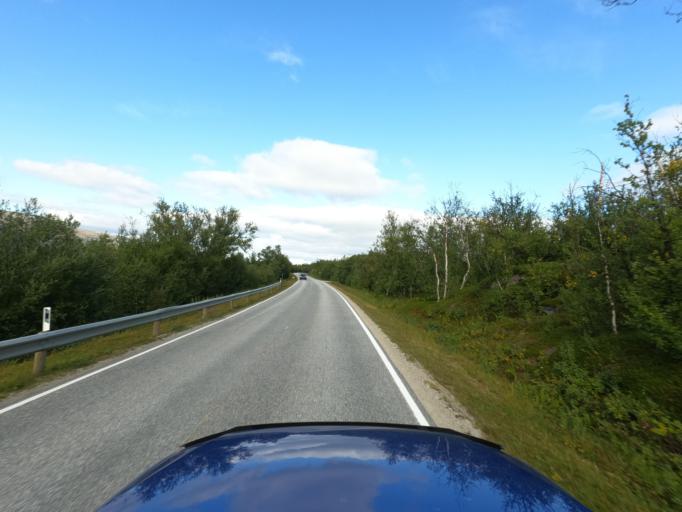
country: NO
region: Finnmark Fylke
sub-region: Porsanger
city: Lakselv
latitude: 70.0200
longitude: 24.9670
